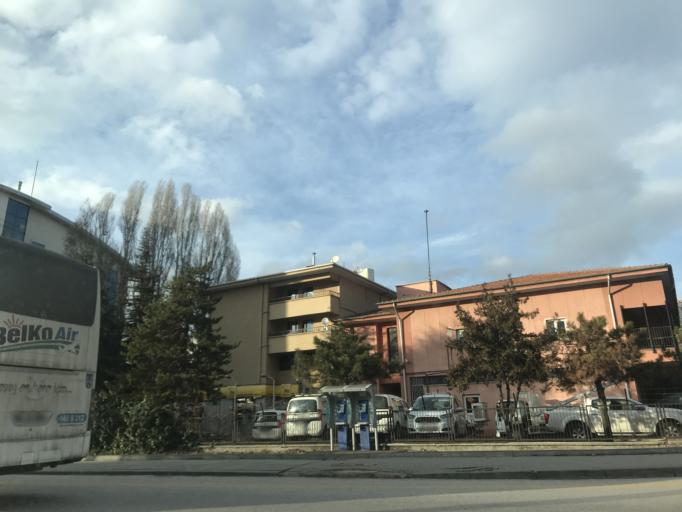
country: TR
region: Ankara
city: Mamak
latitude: 39.9837
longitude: 32.8889
